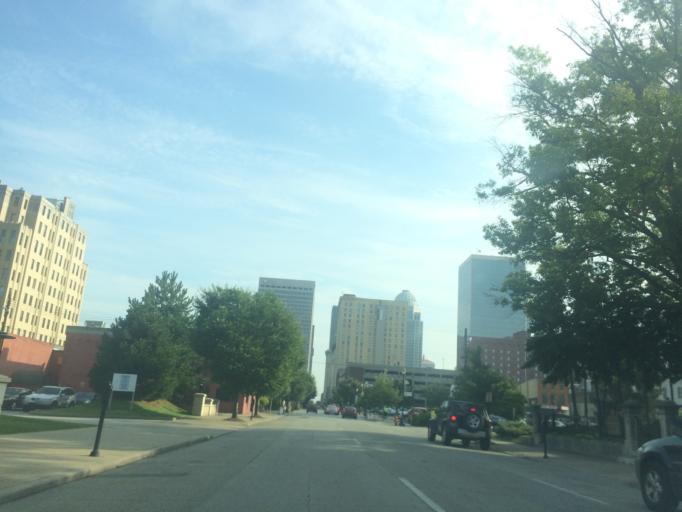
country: US
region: Kentucky
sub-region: Jefferson County
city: Louisville
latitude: 38.2479
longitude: -85.7598
